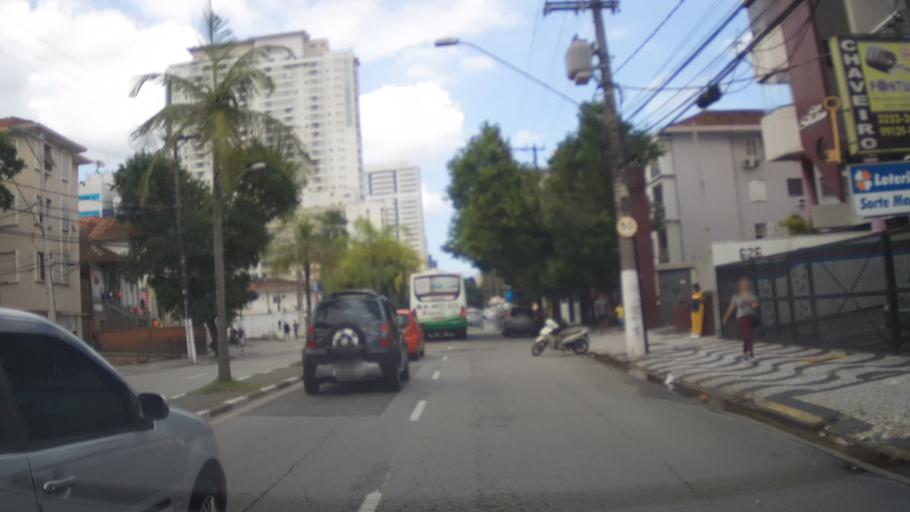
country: BR
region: Sao Paulo
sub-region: Santos
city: Santos
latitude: -23.9612
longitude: -46.3232
